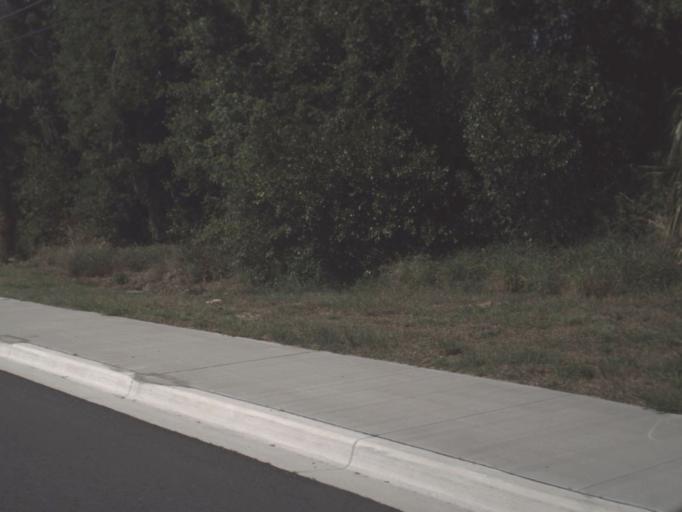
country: US
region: Florida
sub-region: Brevard County
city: Cocoa
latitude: 28.3961
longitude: -80.7499
